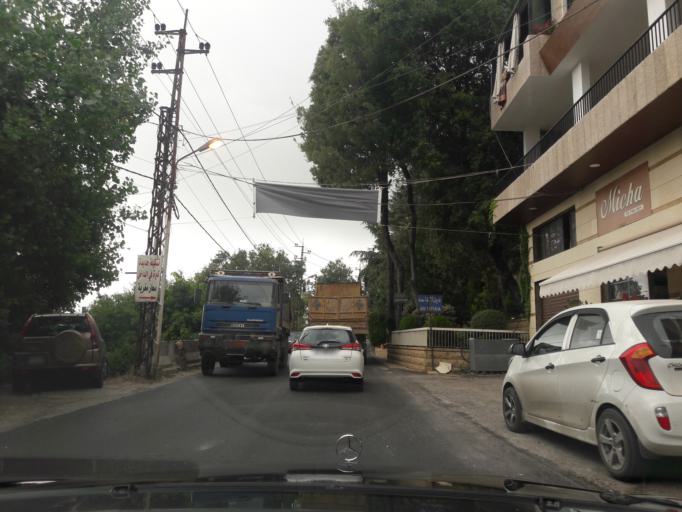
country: LB
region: Mont-Liban
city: Djounie
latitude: 33.9311
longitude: 35.7246
